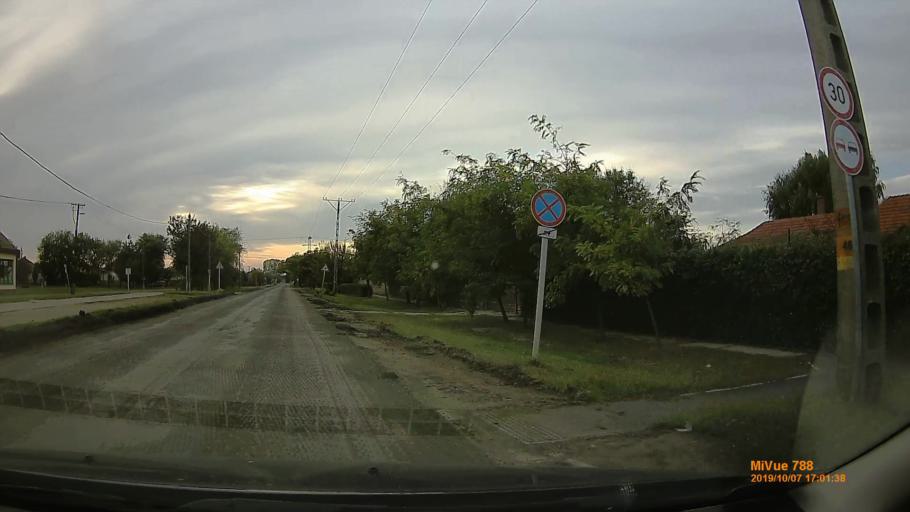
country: HU
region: Bekes
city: Szarvas
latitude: 46.8510
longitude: 20.5626
